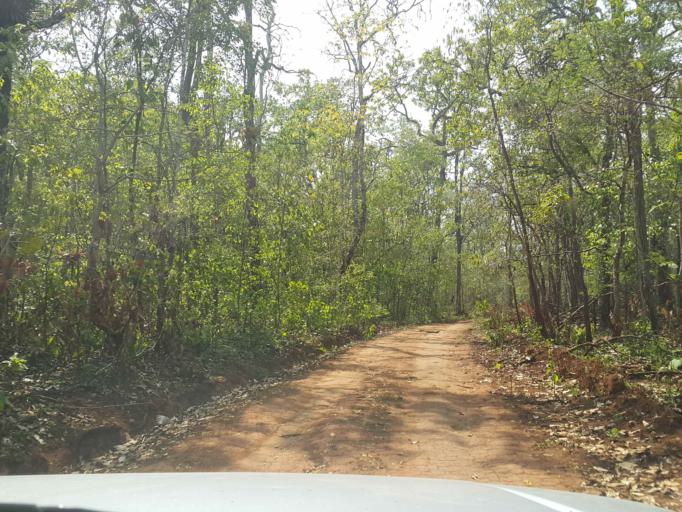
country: TH
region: Chiang Mai
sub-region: Amphoe Chiang Dao
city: Chiang Dao
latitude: 19.3221
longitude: 98.7219
